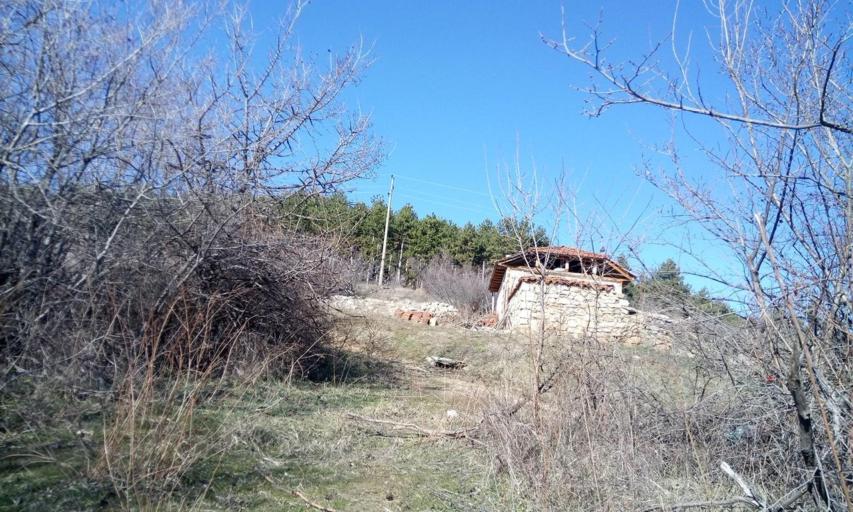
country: BG
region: Plovdiv
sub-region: Obshtina Khisarya
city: Khisarya
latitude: 42.5249
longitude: 24.7186
